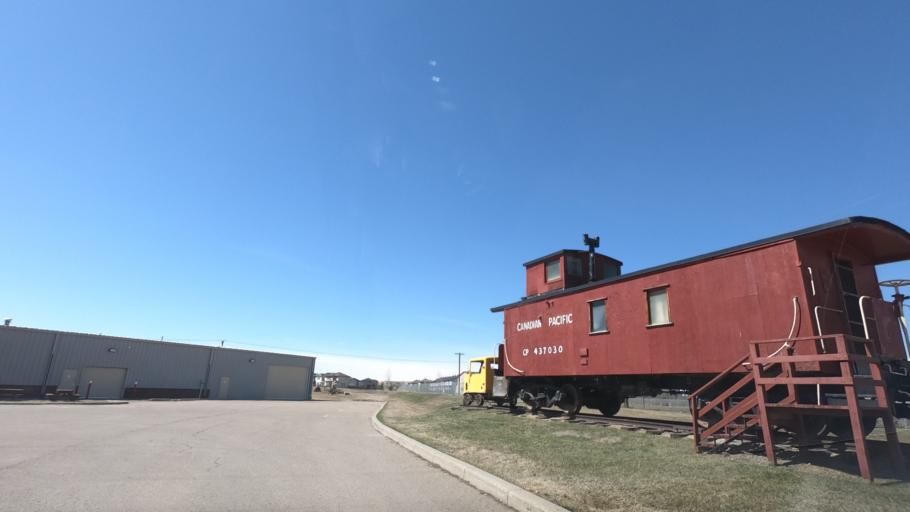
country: CA
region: Alberta
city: Airdrie
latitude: 51.2780
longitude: -114.0133
